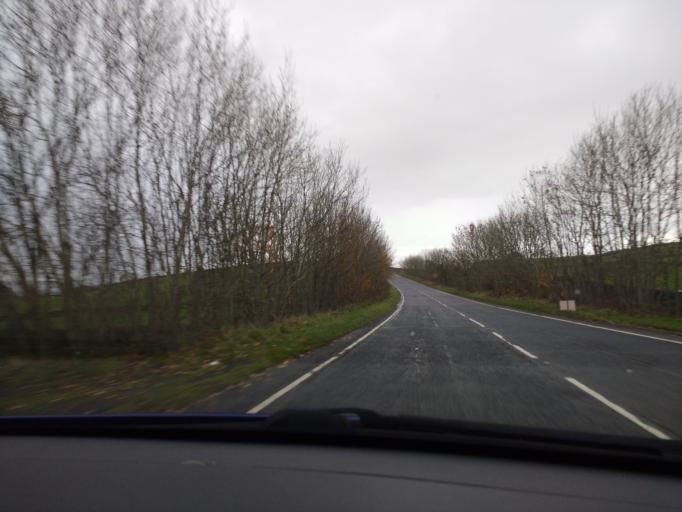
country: GB
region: England
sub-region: Cumbria
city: Millom
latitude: 54.2651
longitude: -3.2617
